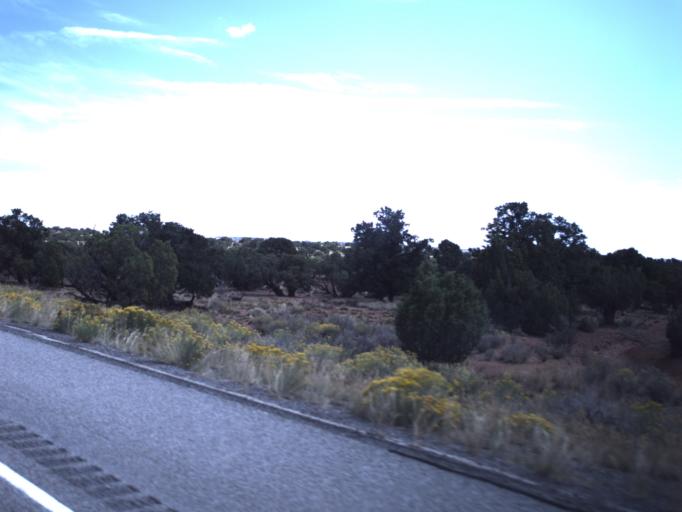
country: US
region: Utah
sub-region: Emery County
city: Castle Dale
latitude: 38.8674
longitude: -110.7154
